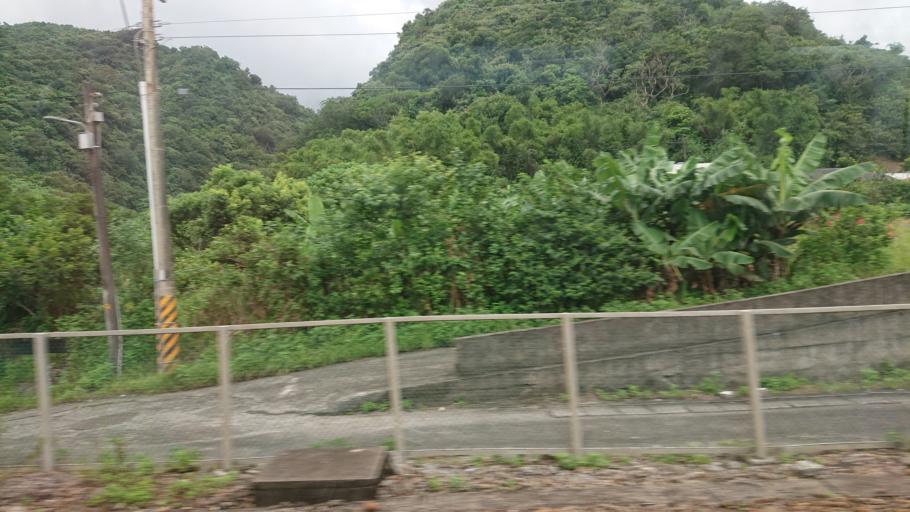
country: TW
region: Taiwan
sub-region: Keelung
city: Keelung
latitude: 24.9509
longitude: 121.9088
